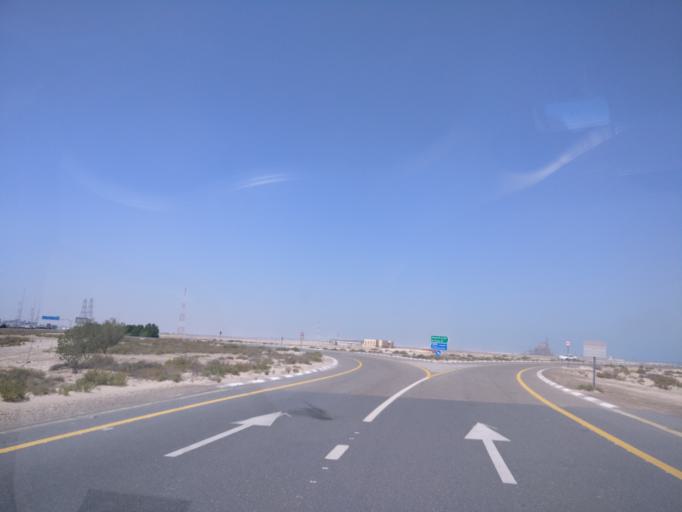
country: AE
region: Dubai
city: Dubai
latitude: 24.9078
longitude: 54.9513
